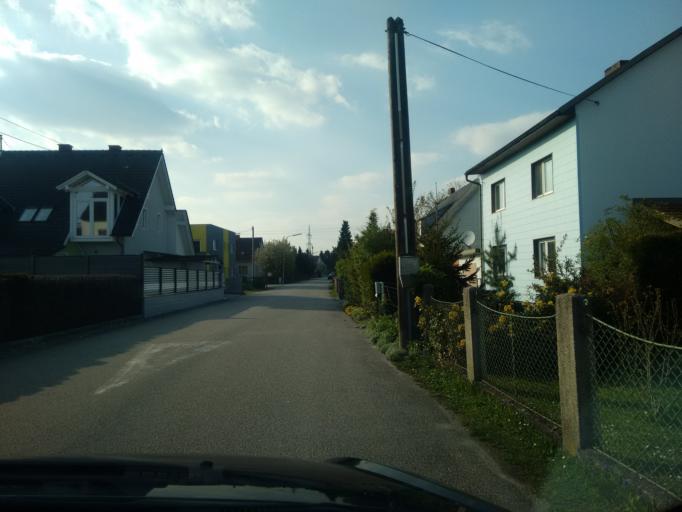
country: AT
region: Upper Austria
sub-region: Politischer Bezirk Linz-Land
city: Traun
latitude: 48.2298
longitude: 14.2497
